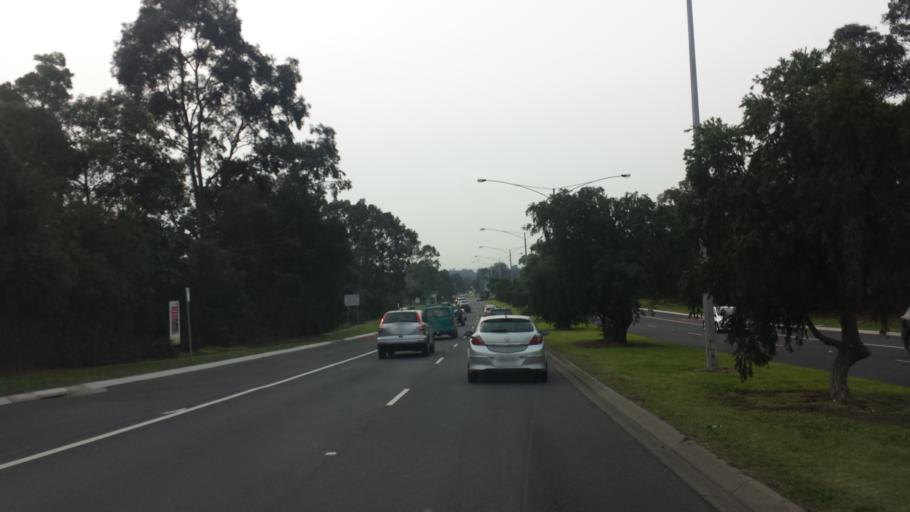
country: AU
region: Victoria
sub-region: Banyule
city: Darch
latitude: -37.7579
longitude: 145.1342
